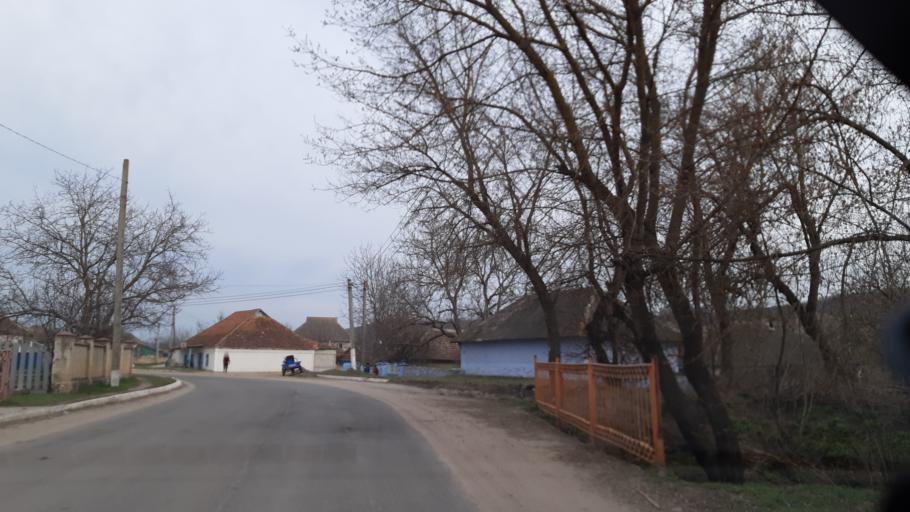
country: MD
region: Soldanesti
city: Soldanesti
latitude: 47.6840
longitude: 28.7590
